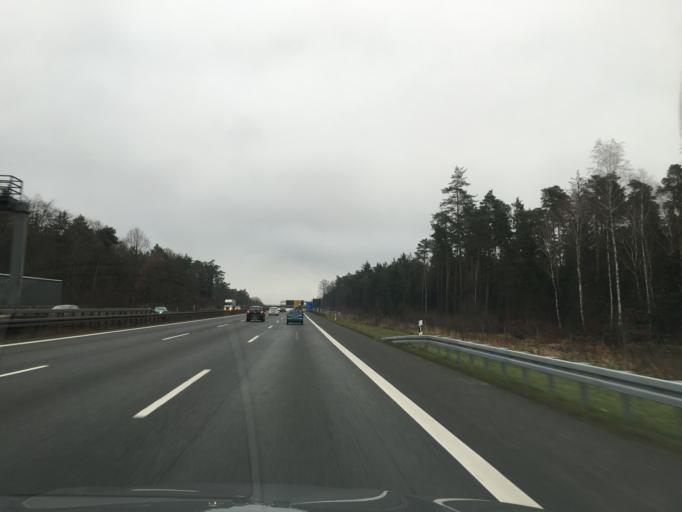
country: DE
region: Bavaria
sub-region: Regierungsbezirk Mittelfranken
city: Schwaig
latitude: 49.4325
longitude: 11.2174
